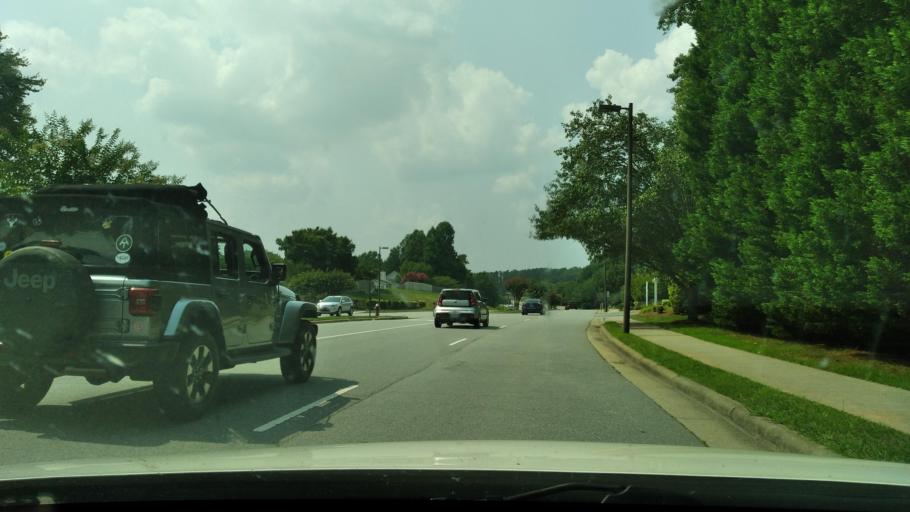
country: US
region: North Carolina
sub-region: Guilford County
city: Jamestown
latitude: 36.0407
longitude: -79.9231
